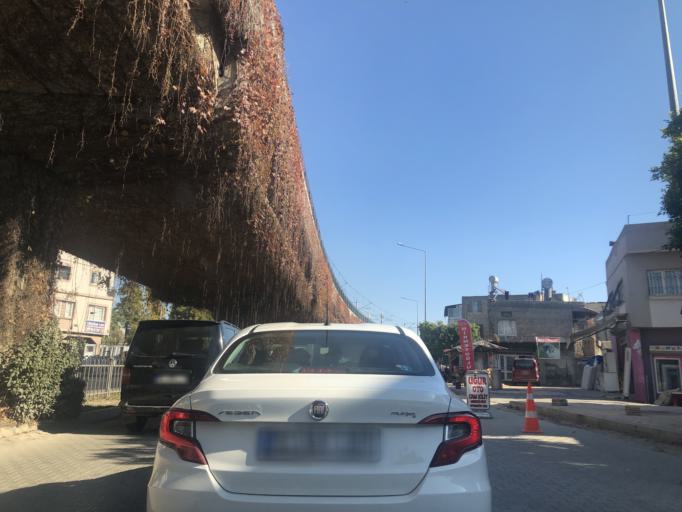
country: TR
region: Adana
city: Adana
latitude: 36.9796
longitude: 35.3300
